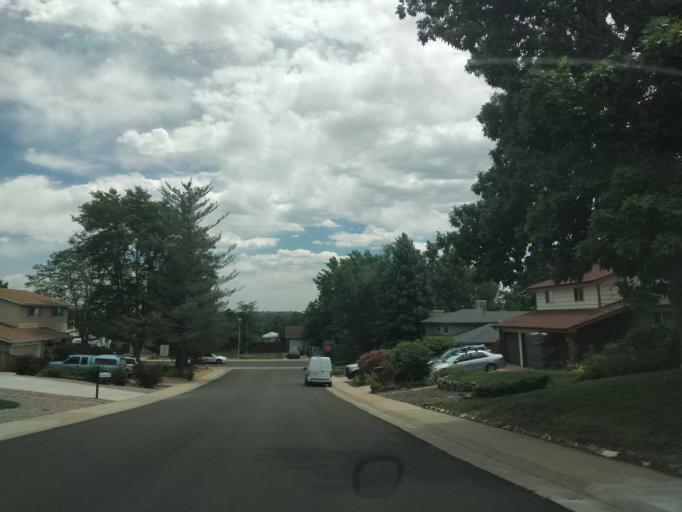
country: US
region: Colorado
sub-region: Jefferson County
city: Lakewood
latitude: 39.6730
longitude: -105.0996
